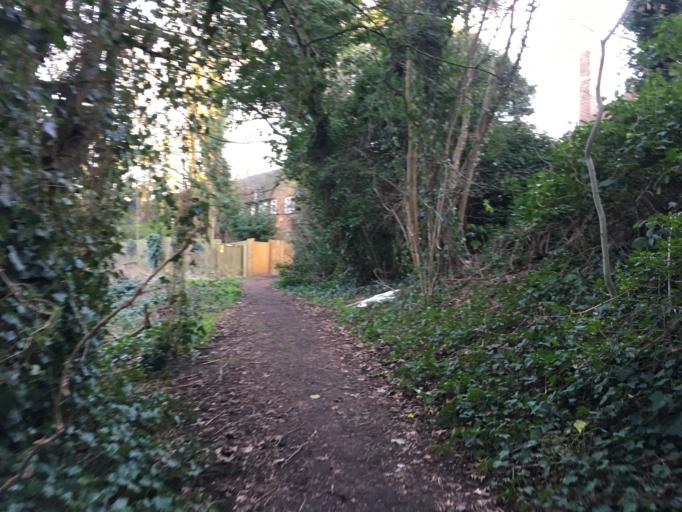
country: GB
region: England
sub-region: Greater London
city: Hendon
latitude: 51.5878
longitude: -0.1941
